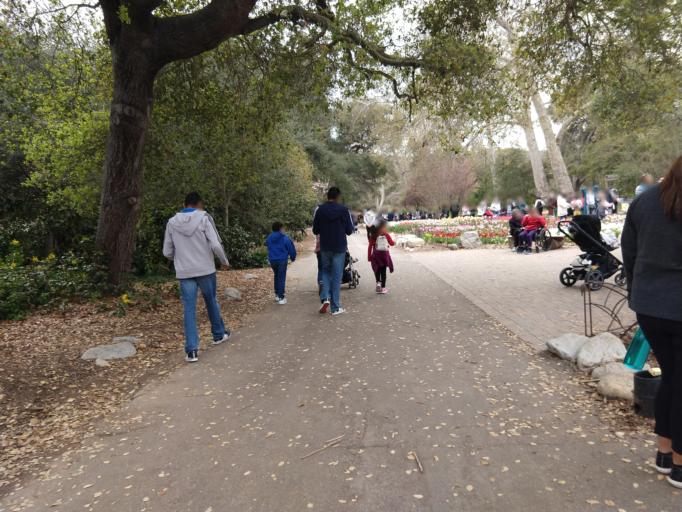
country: US
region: California
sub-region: Los Angeles County
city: La Canada Flintridge
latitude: 34.2012
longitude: -118.2110
